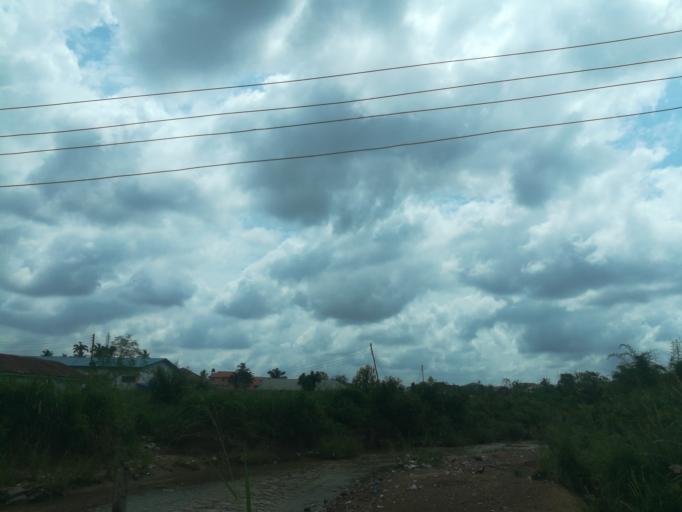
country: NG
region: Oyo
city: Ibadan
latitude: 7.3684
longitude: 3.8241
